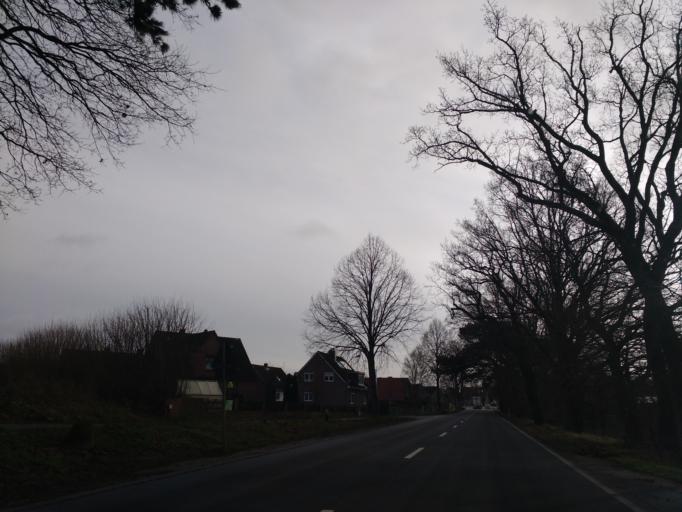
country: DE
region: Schleswig-Holstein
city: Ratekau
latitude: 53.9923
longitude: 10.7097
